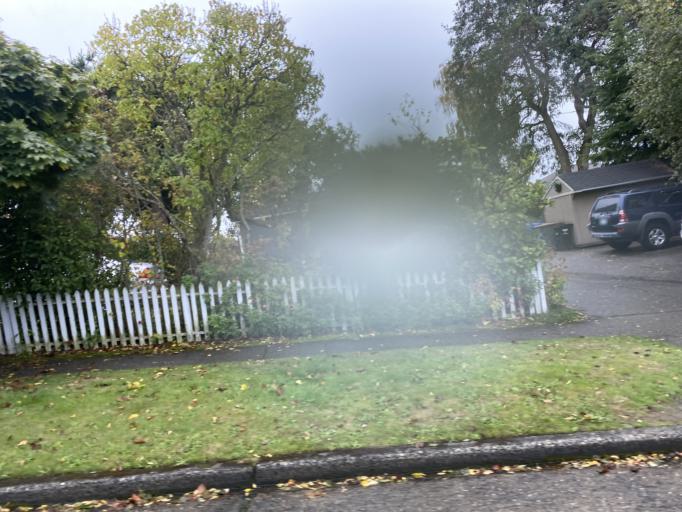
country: US
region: Washington
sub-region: King County
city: Seattle
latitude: 47.6432
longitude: -122.3962
